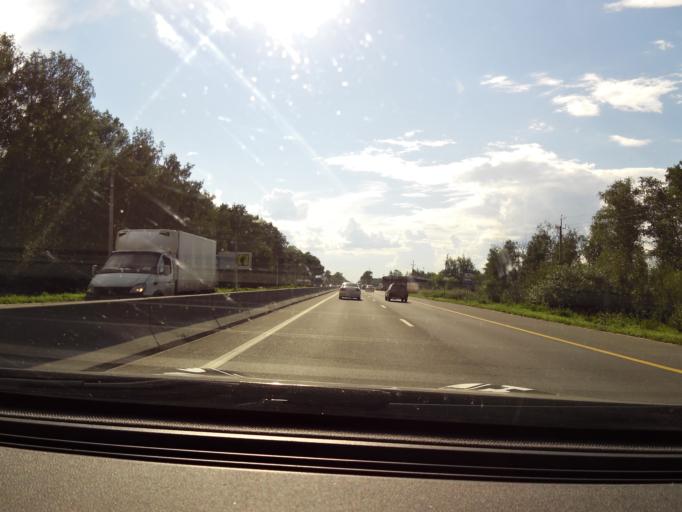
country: RU
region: Nizjnij Novgorod
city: Gorbatovka
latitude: 56.3097
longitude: 43.7666
